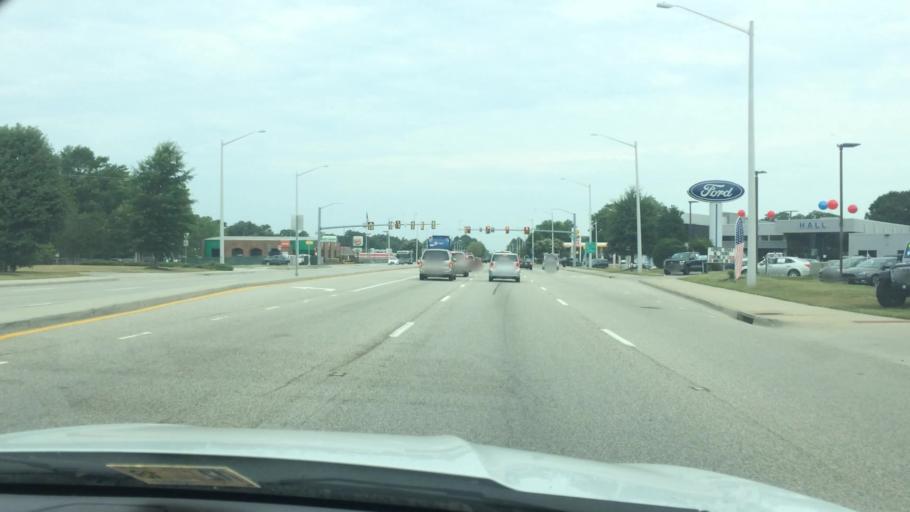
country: US
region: Virginia
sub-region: York County
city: Yorktown
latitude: 37.1477
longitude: -76.5270
